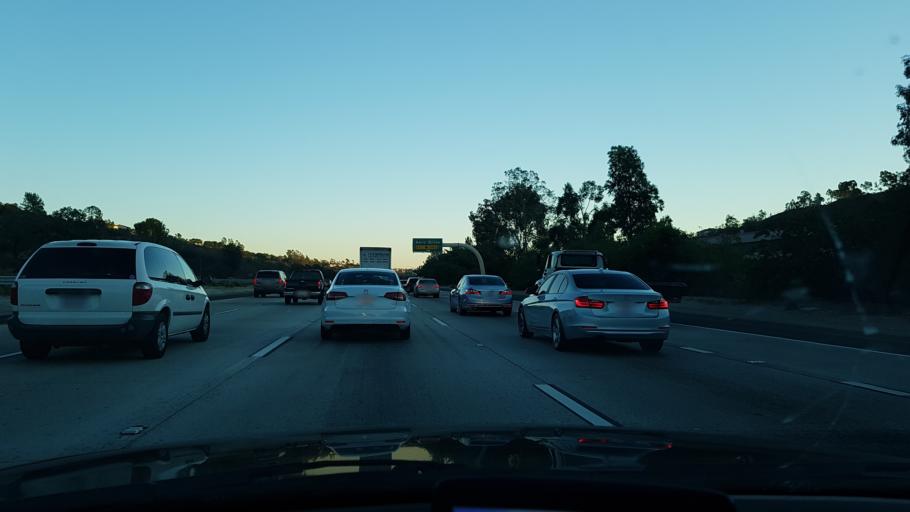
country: US
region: California
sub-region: San Diego County
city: La Mesa
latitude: 32.8175
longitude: -117.1157
